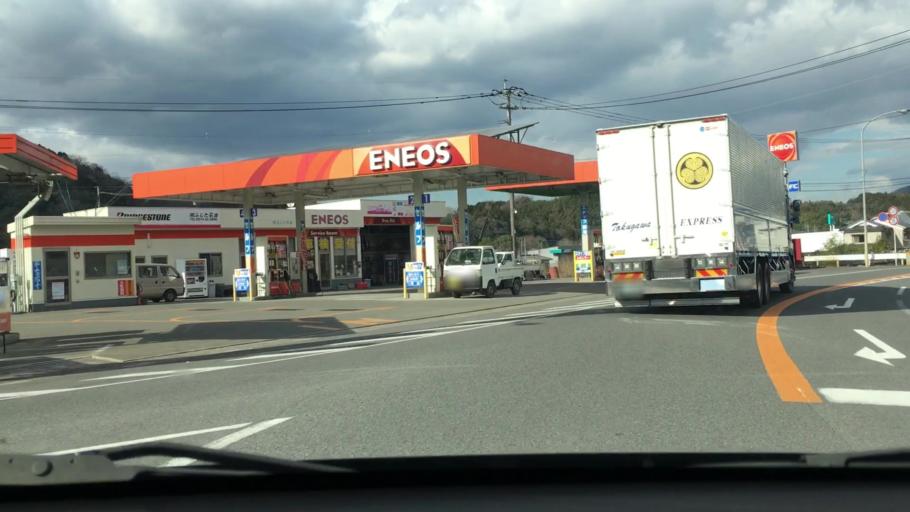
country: JP
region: Oita
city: Usuki
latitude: 33.0329
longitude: 131.6892
